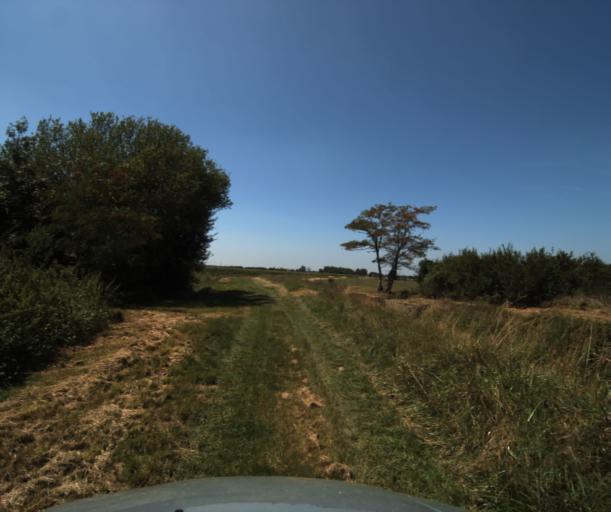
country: FR
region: Midi-Pyrenees
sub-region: Departement de la Haute-Garonne
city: Labastidette
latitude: 43.4619
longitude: 1.2766
